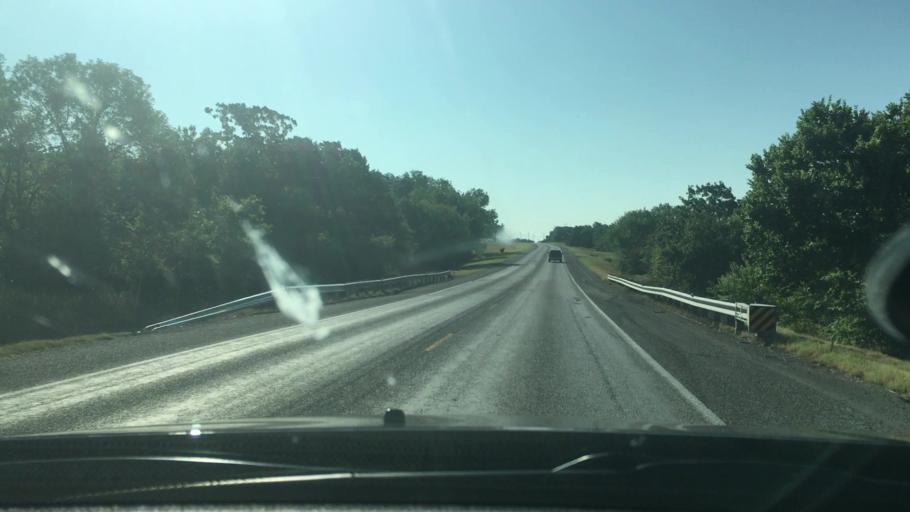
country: US
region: Oklahoma
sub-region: Johnston County
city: Tishomingo
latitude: 34.2394
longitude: -96.7393
